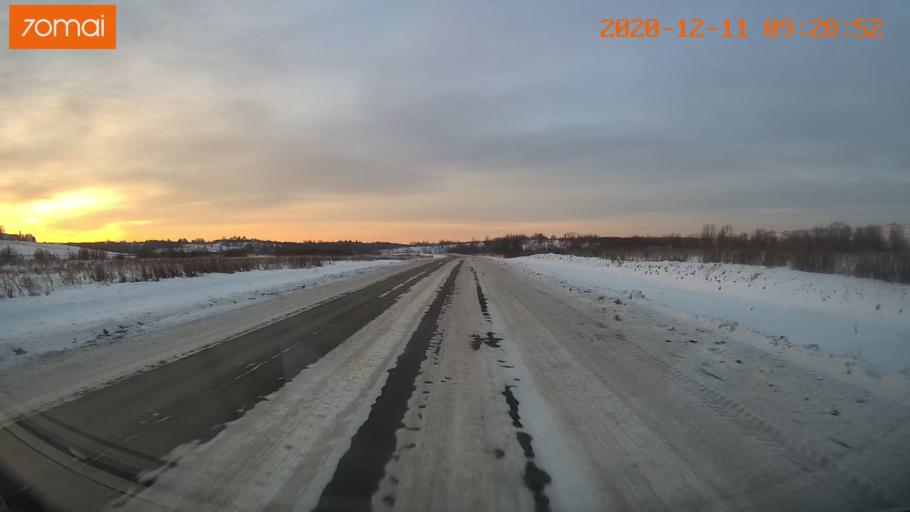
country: RU
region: Vologda
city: Vologda
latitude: 59.1487
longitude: 40.0054
